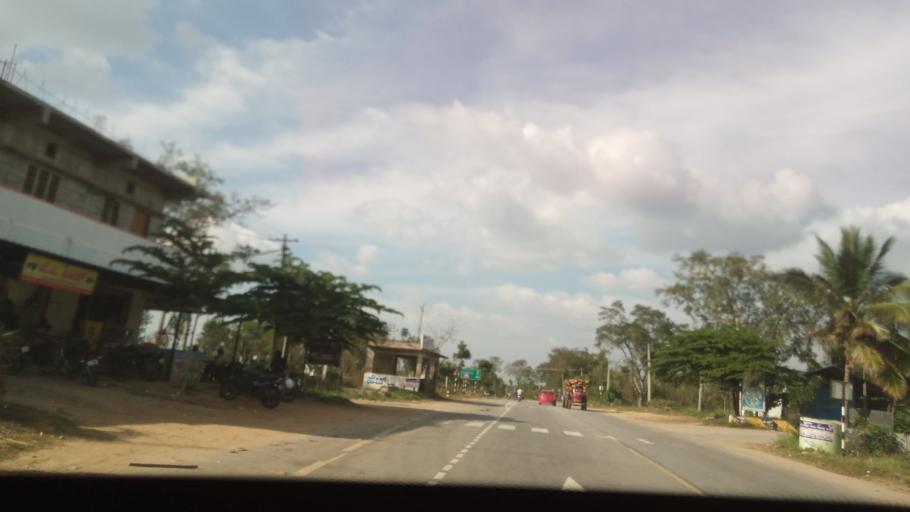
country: IN
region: Karnataka
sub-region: Mandya
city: Maddur
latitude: 12.6371
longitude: 77.0568
